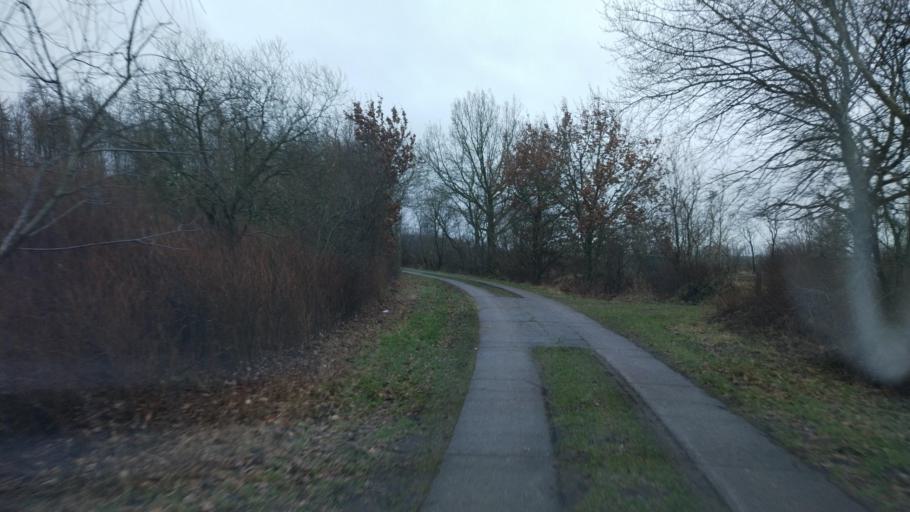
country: DE
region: Schleswig-Holstein
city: Gross Rheide
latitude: 54.4645
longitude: 9.4276
